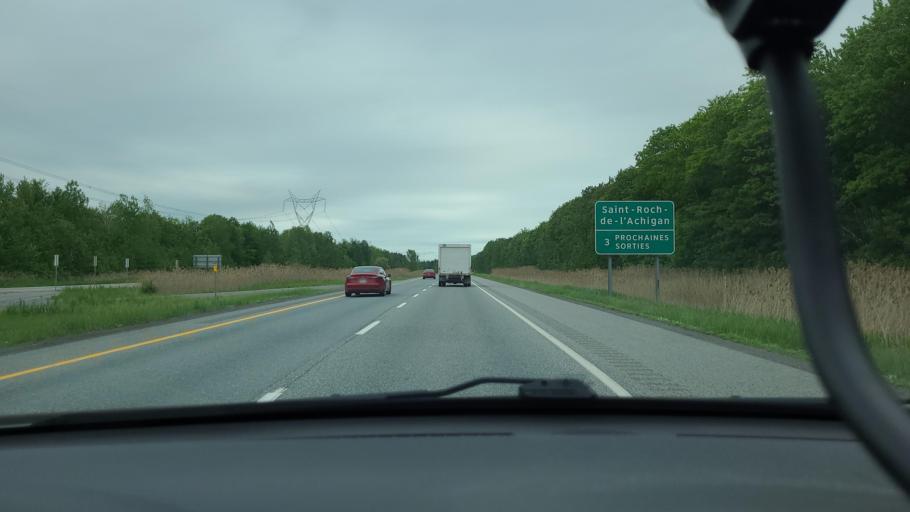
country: CA
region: Quebec
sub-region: Lanaudiere
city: Mascouche
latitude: 45.8044
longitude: -73.5889
